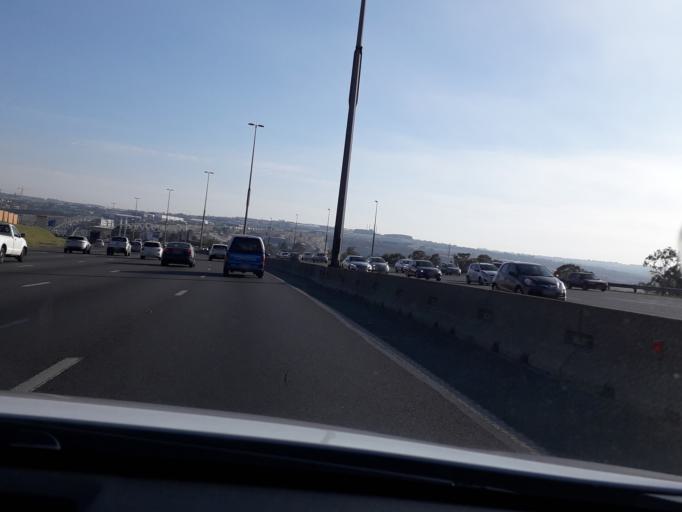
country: ZA
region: Gauteng
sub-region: City of Johannesburg Metropolitan Municipality
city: Midrand
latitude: -26.0394
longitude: 28.1056
